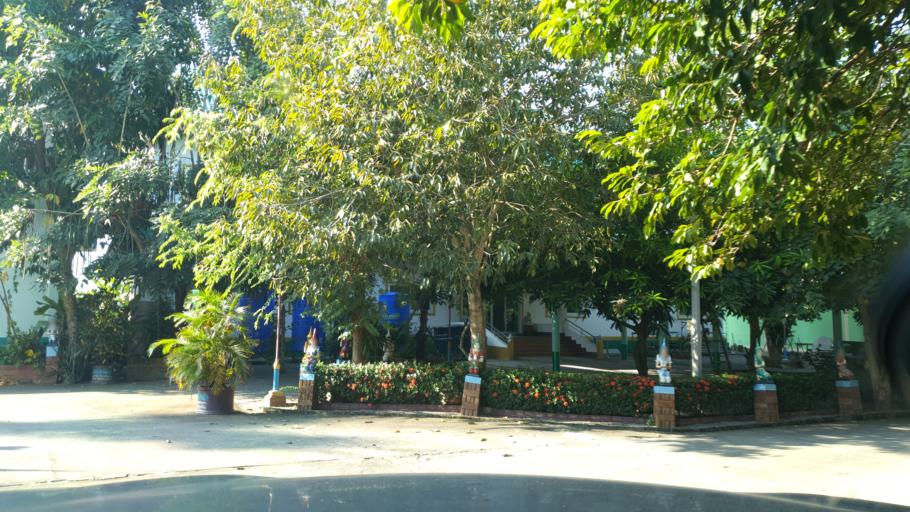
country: TH
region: Chiang Mai
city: Mae On
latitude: 18.7245
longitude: 99.2000
